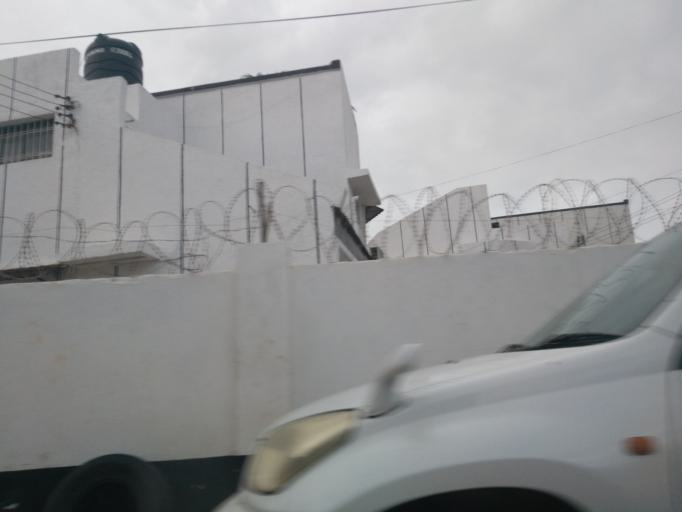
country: TZ
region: Dar es Salaam
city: Magomeni
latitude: -6.7584
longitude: 39.2714
